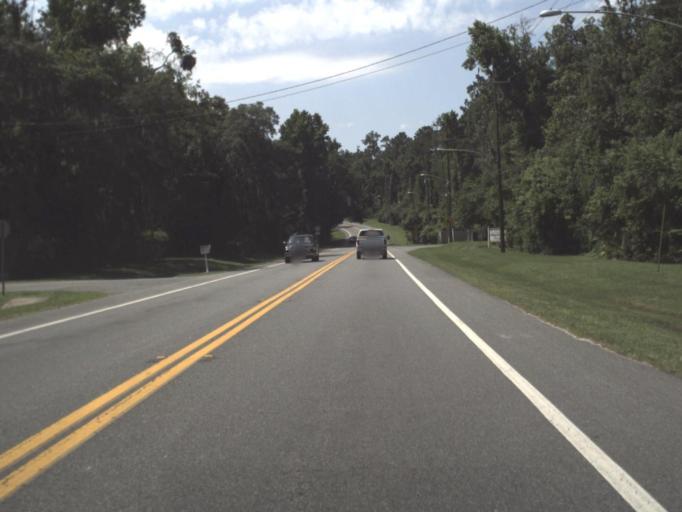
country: US
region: Florida
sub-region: Alachua County
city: Gainesville
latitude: 29.6342
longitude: -82.3265
